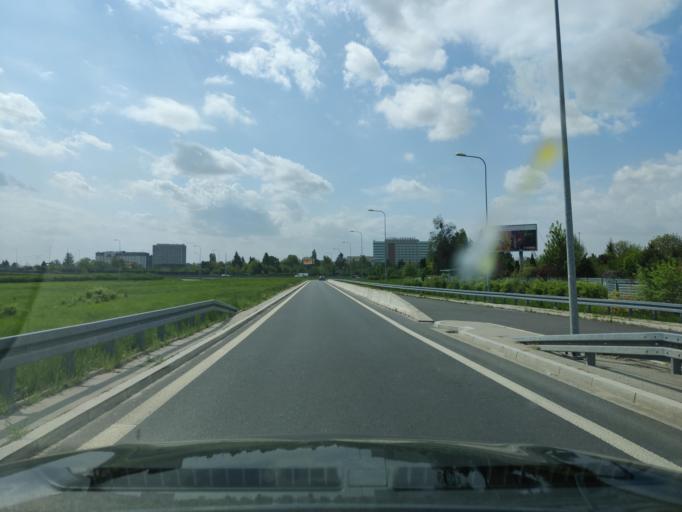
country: PL
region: Masovian Voivodeship
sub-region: Warszawa
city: Ochota
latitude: 52.1844
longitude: 20.9845
